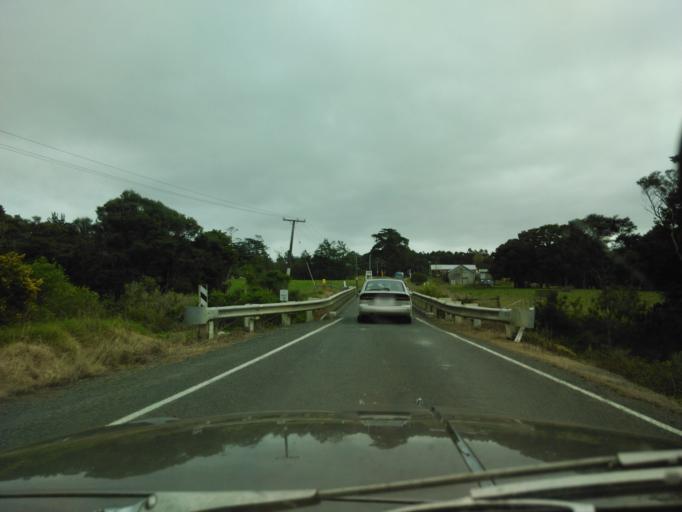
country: NZ
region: Auckland
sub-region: Auckland
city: Wellsford
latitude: -36.1391
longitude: 174.5124
